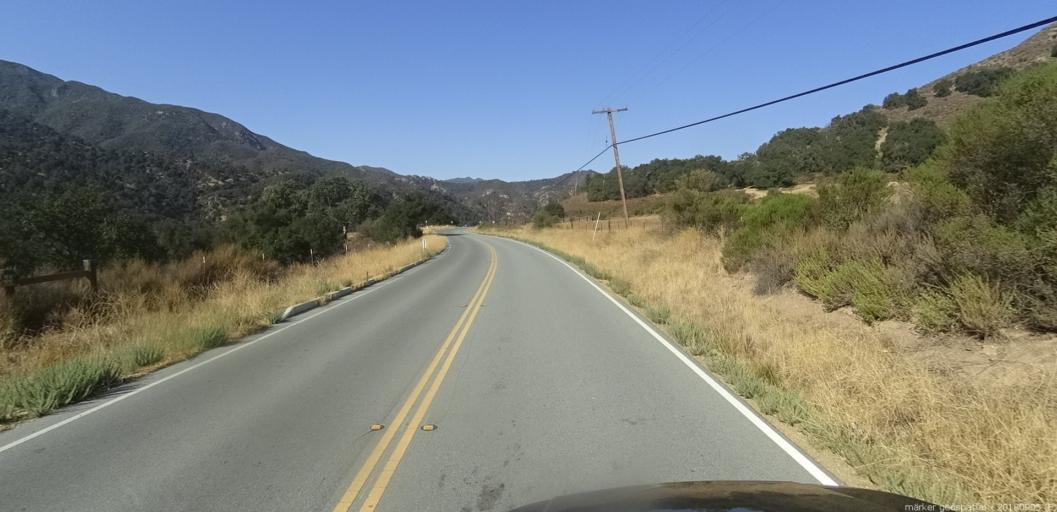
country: US
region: California
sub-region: Monterey County
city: Greenfield
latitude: 36.2331
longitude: -121.4568
